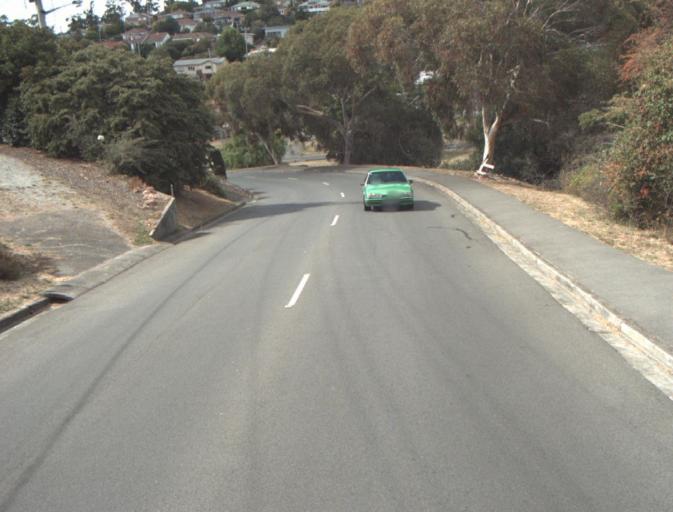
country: AU
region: Tasmania
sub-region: Launceston
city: Launceston
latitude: -41.4356
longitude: 147.1154
